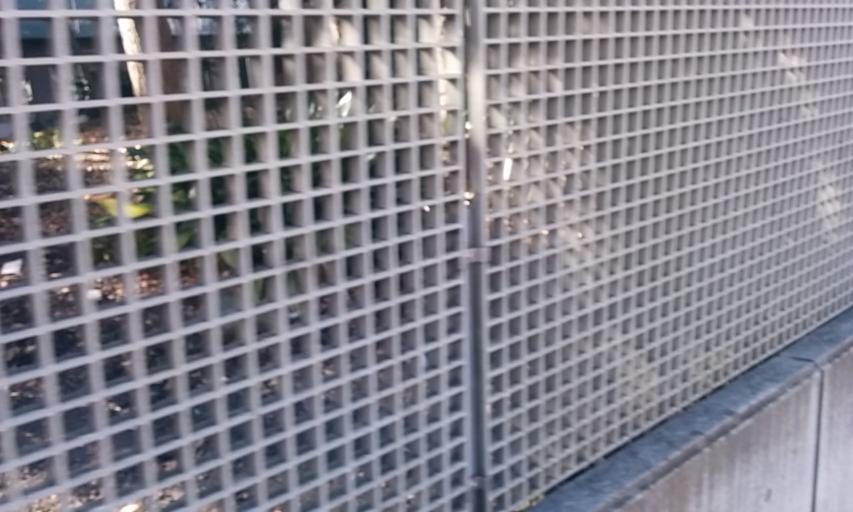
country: JP
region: Tokyo
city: Urayasu
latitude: 35.7161
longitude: 139.7970
